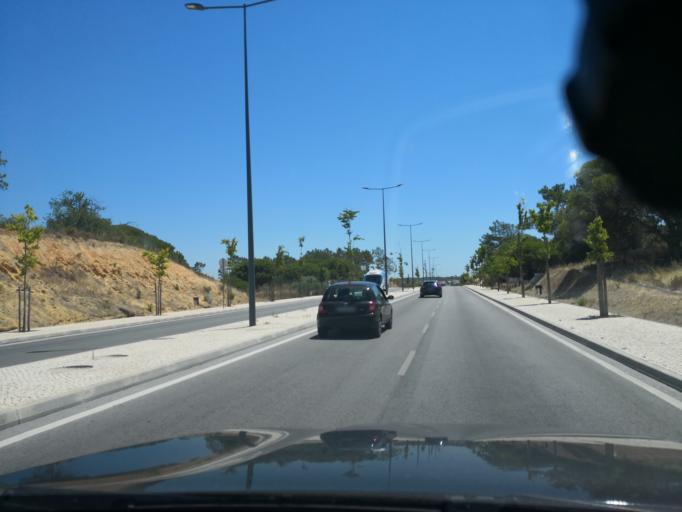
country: PT
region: Faro
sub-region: Loule
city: Quarteira
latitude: 37.0736
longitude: -8.0934
